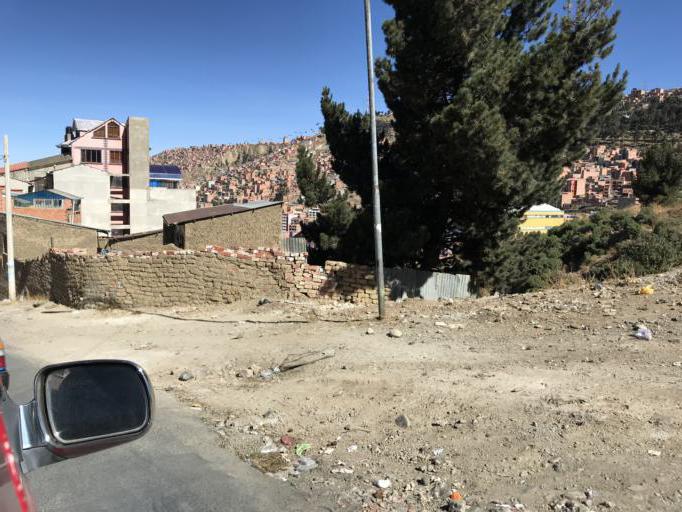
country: BO
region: La Paz
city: La Paz
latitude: -16.4873
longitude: -68.1644
